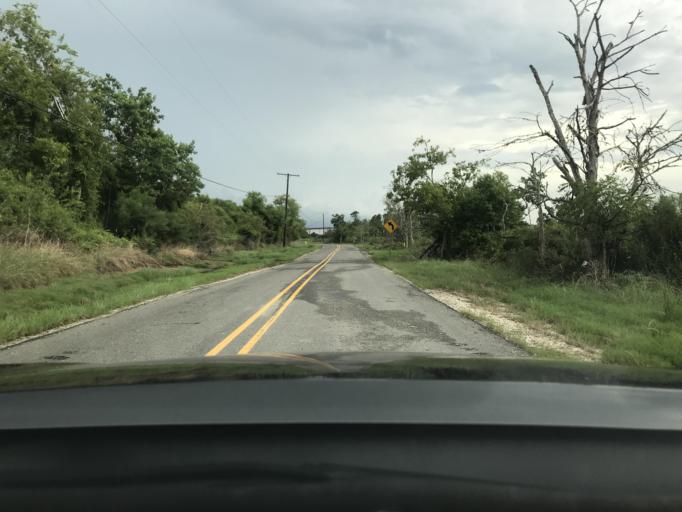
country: US
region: Louisiana
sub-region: Calcasieu Parish
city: Westlake
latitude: 30.2234
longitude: -93.2509
